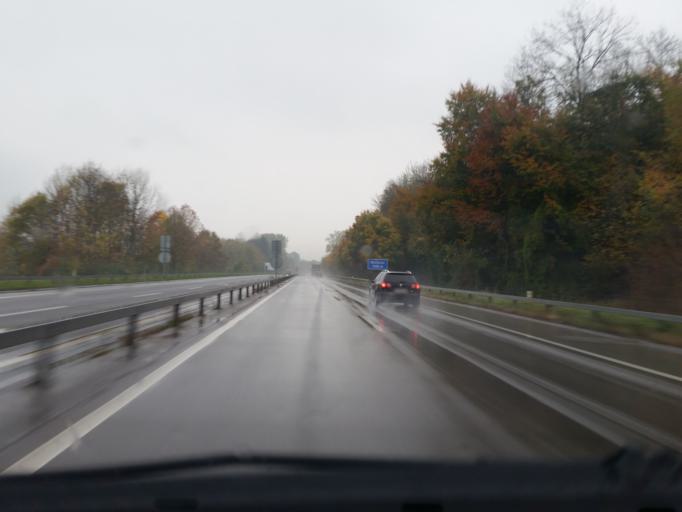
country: CH
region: Thurgau
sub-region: Weinfelden District
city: Wigoltingen
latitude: 47.5827
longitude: 9.0177
